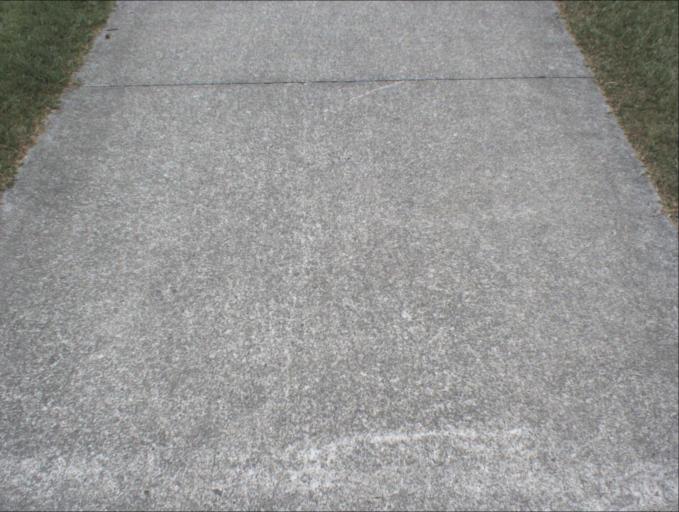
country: AU
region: Queensland
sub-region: Logan
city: Slacks Creek
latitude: -27.6442
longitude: 153.1691
